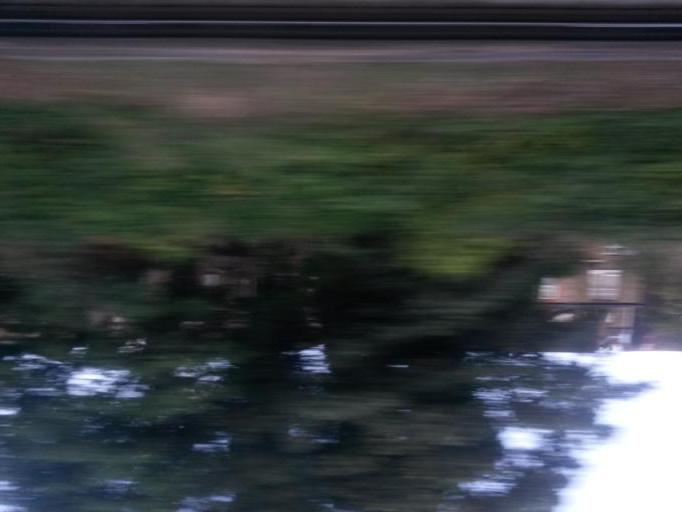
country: GB
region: England
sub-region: Greater London
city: Brixton Hill
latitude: 51.4289
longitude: -0.1383
